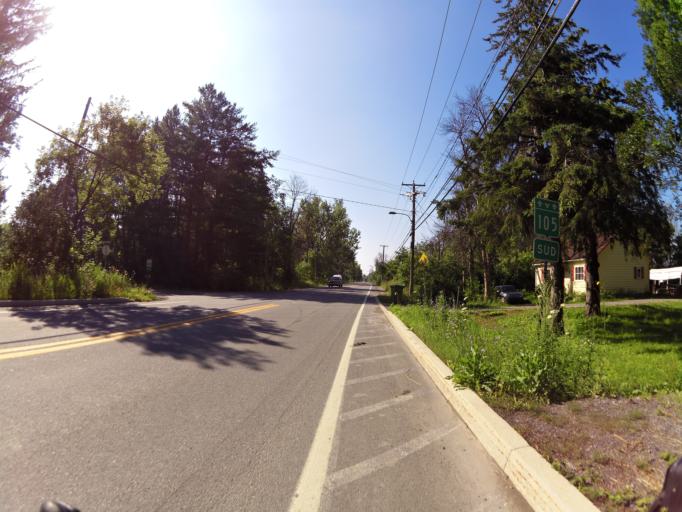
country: CA
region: Quebec
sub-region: Outaouais
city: Gatineau
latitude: 45.5034
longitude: -75.7829
